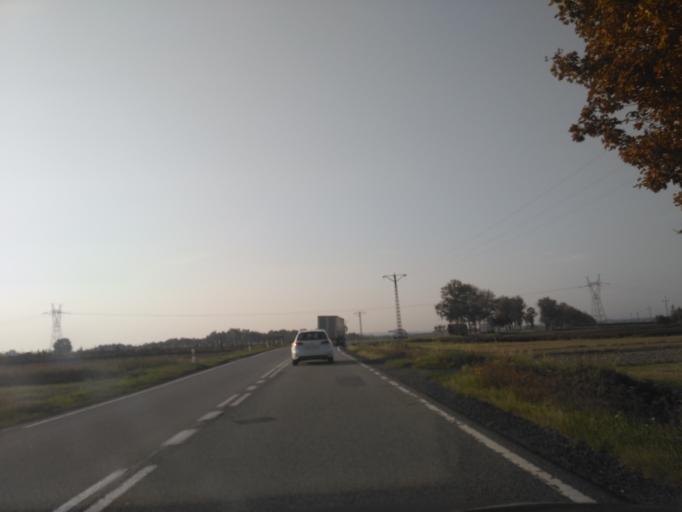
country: PL
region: Lublin Voivodeship
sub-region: Powiat krasnicki
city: Szastarka
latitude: 50.8171
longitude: 22.3183
